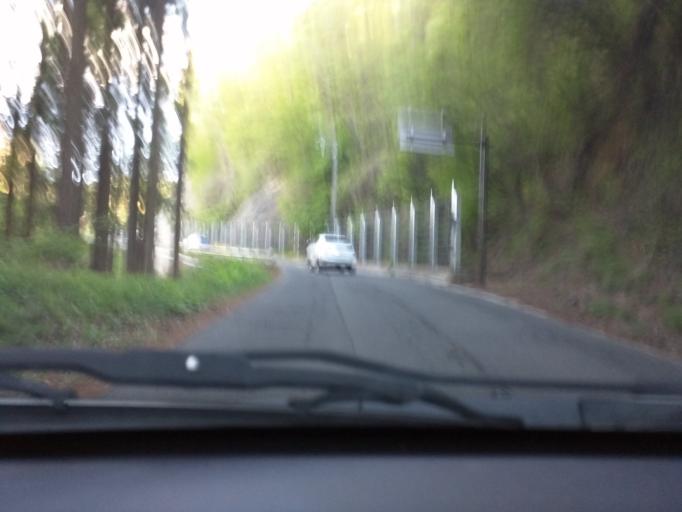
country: JP
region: Nagano
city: Nagano-shi
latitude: 36.6757
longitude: 138.1735
